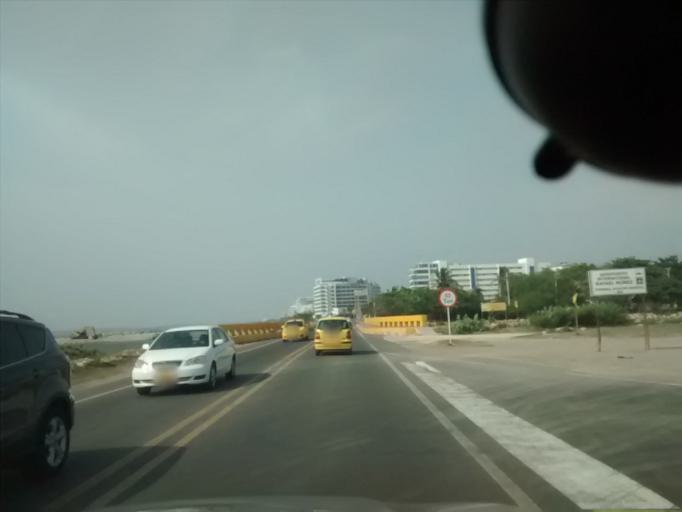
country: CO
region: Bolivar
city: Cartagena
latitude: 10.4551
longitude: -75.5119
